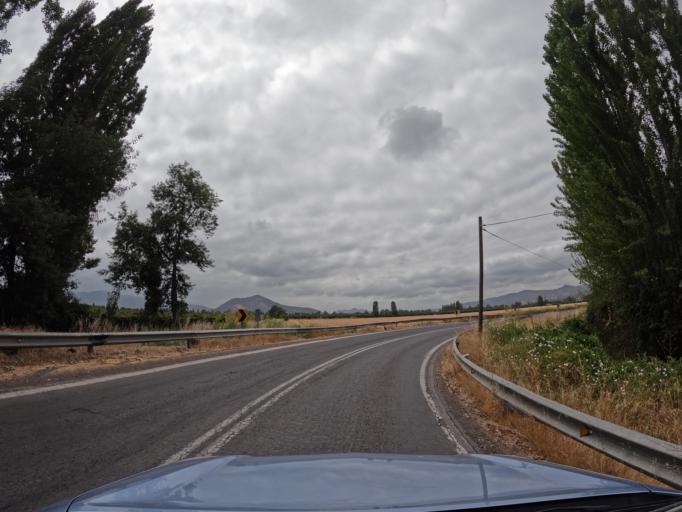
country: CL
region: Maule
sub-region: Provincia de Curico
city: Teno
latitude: -34.7518
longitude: -71.2179
